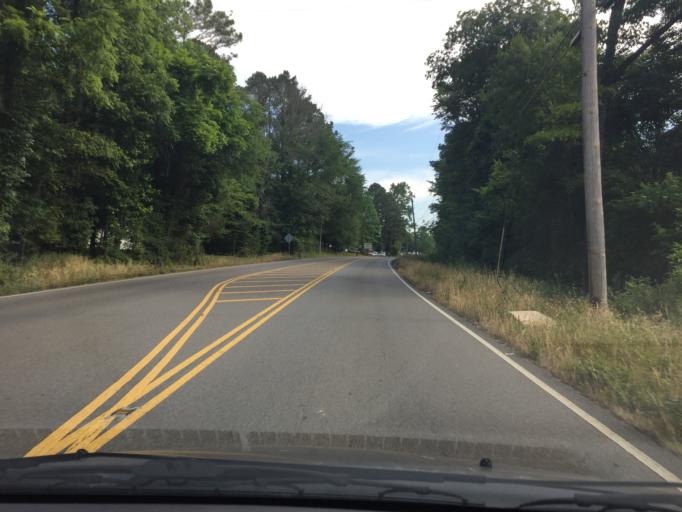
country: US
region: Tennessee
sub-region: Hamilton County
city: Collegedale
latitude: 35.0979
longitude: -85.0076
